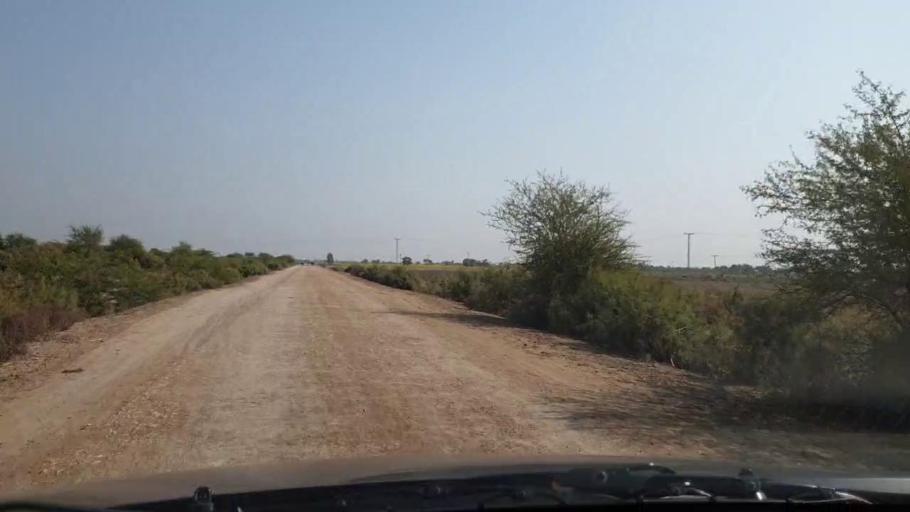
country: PK
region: Sindh
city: Jhol
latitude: 25.9961
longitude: 68.9205
